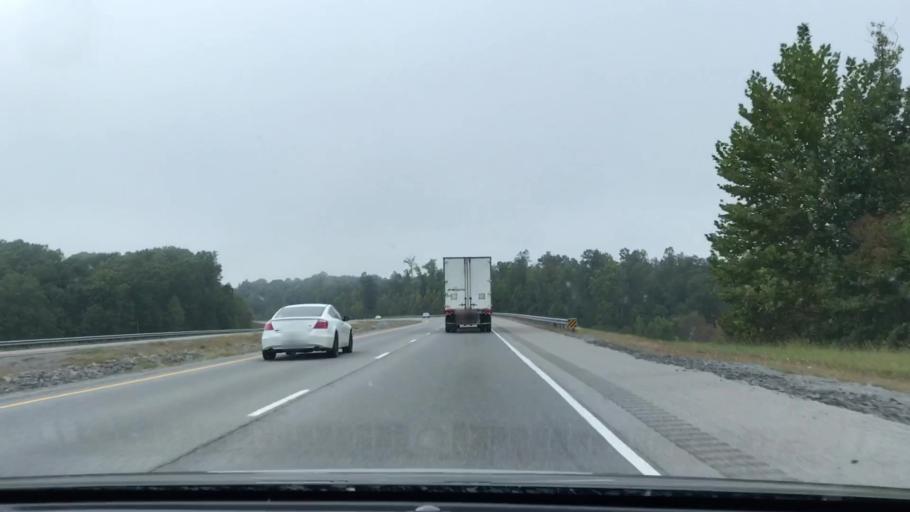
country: US
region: Tennessee
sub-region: Sumner County
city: Gallatin
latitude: 36.4824
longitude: -86.4799
